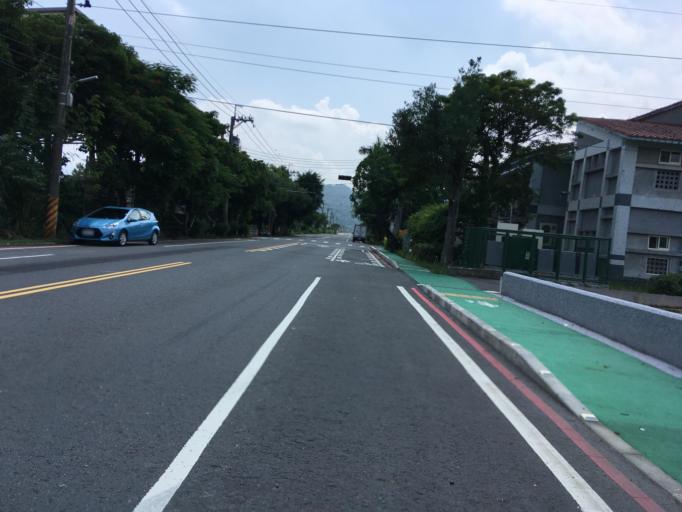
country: TW
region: Taiwan
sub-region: Yilan
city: Yilan
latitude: 24.6803
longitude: 121.6890
